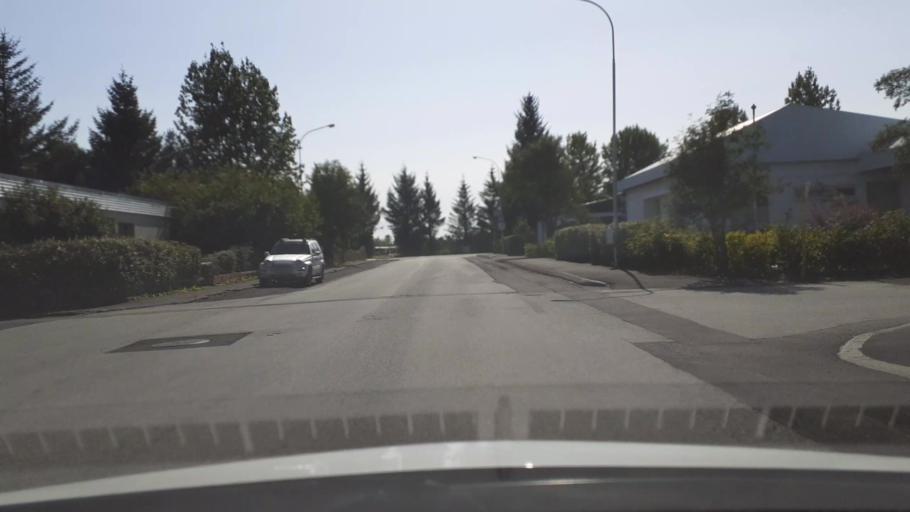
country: IS
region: South
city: Selfoss
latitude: 63.9346
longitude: -20.9871
